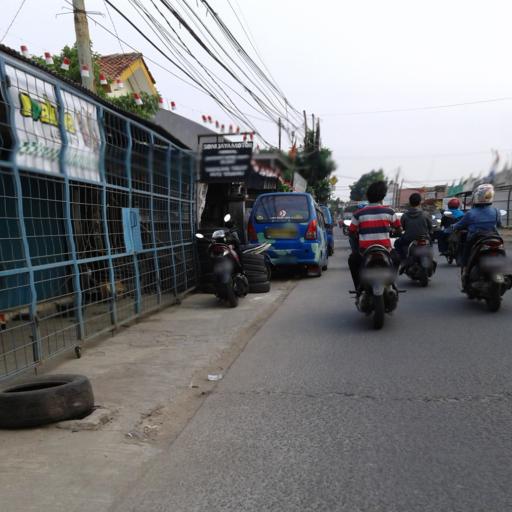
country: ID
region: West Java
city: Sawangan
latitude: -6.3875
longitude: 106.7688
